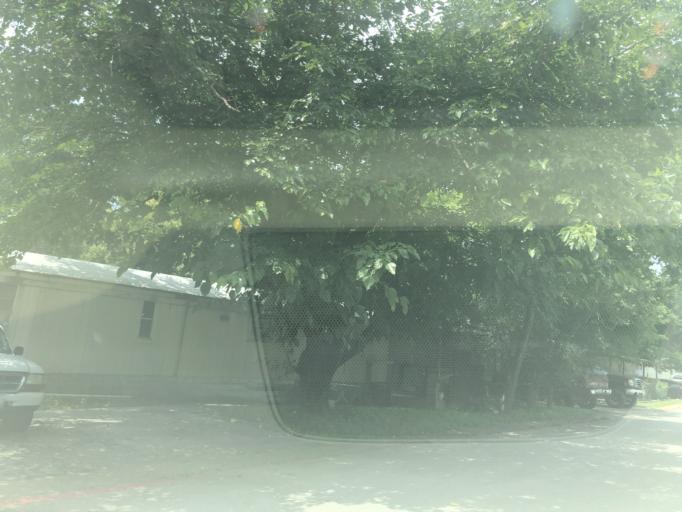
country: US
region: Texas
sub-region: Dallas County
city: Irving
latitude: 32.7932
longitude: -96.9300
